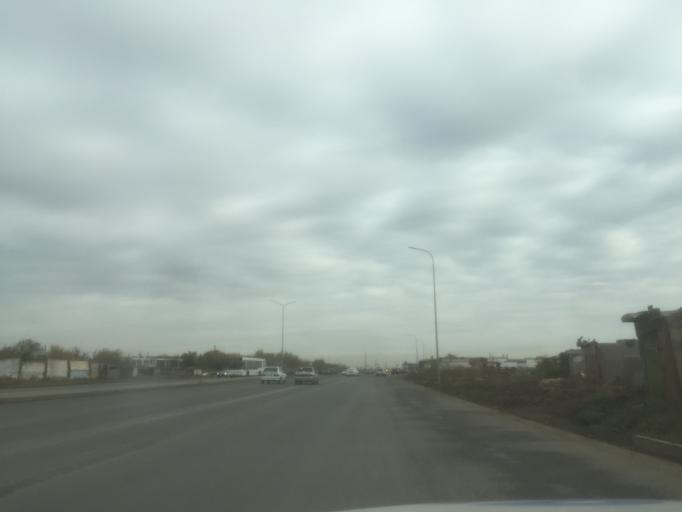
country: KZ
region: Astana Qalasy
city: Astana
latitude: 51.1758
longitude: 71.3798
